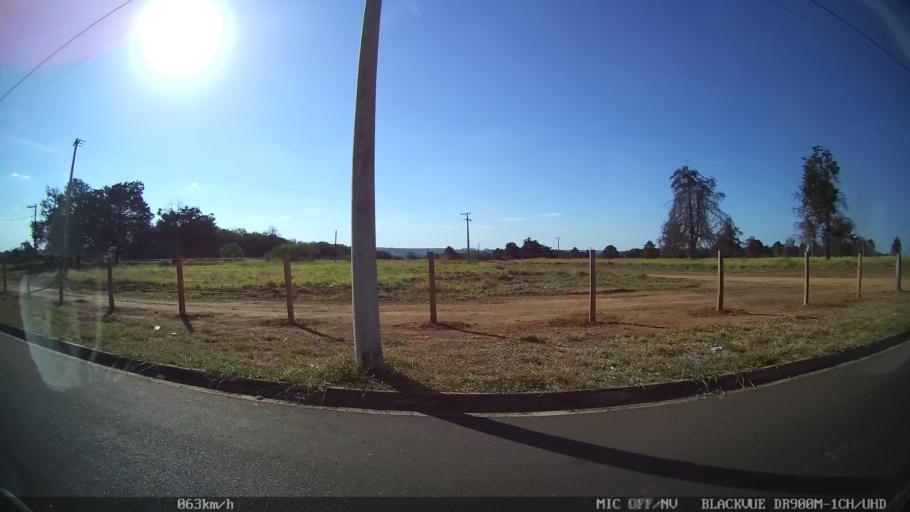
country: BR
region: Sao Paulo
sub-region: Franca
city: Franca
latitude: -20.5064
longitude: -47.4408
